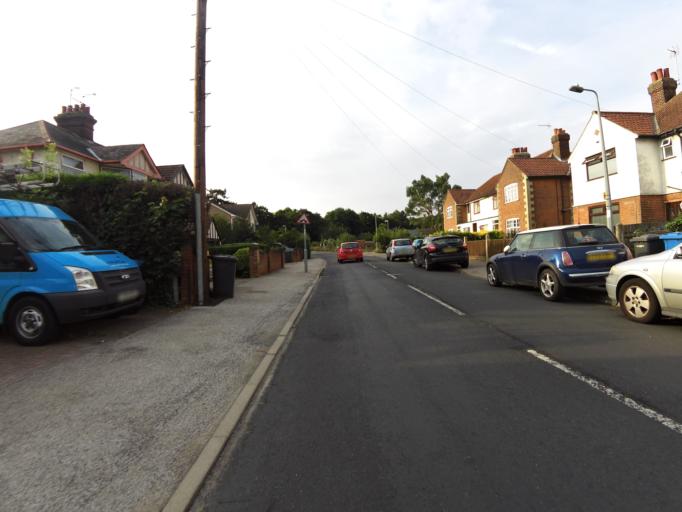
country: GB
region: England
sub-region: Suffolk
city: Ipswich
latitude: 52.0655
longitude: 1.1724
